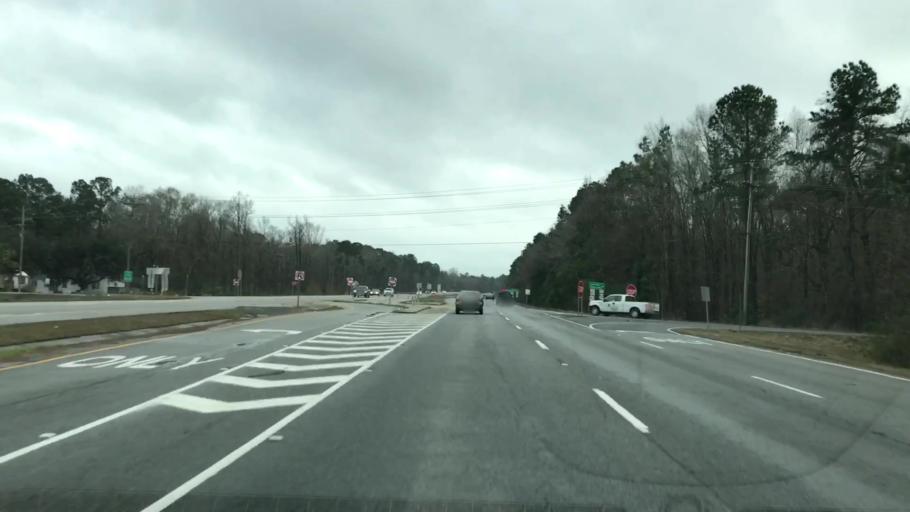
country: US
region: South Carolina
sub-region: Berkeley County
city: Moncks Corner
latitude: 33.1265
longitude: -80.0297
